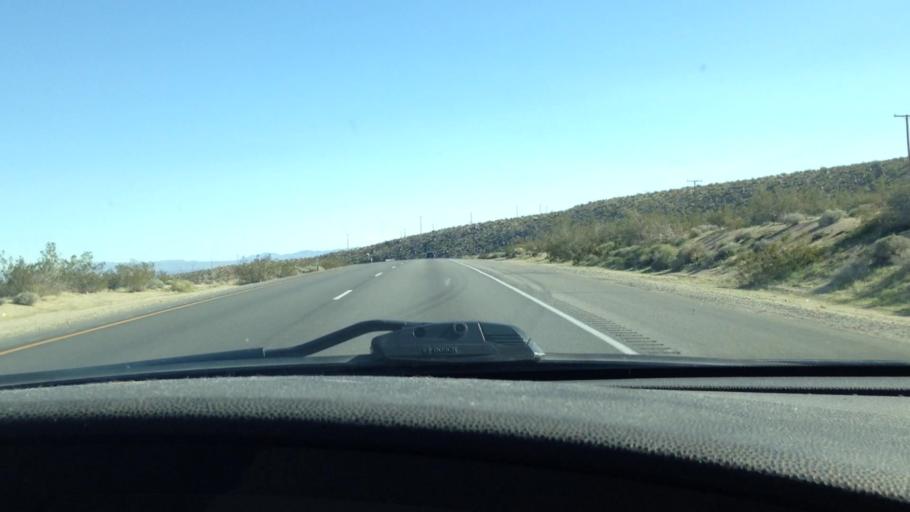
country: US
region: California
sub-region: Kern County
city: Inyokern
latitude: 35.8756
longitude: -117.8890
